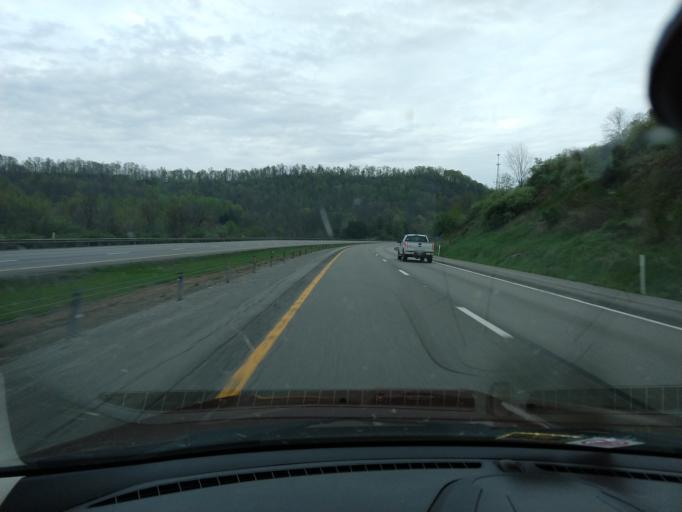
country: US
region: West Virginia
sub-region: Lewis County
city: Weston
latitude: 39.0116
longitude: -80.4945
